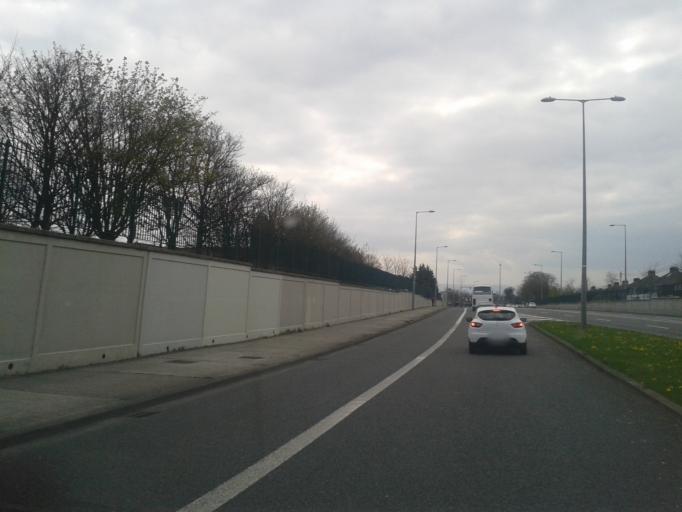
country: IE
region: Leinster
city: Beaumont
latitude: 53.3862
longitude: -6.2425
